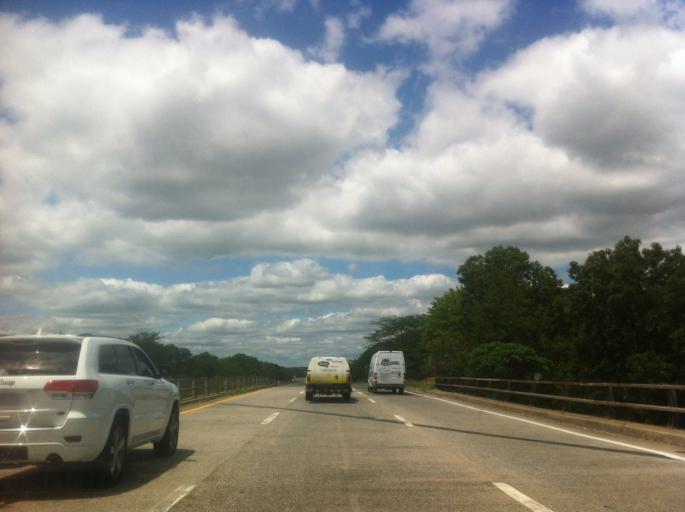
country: US
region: New York
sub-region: Suffolk County
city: Shirley
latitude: 40.8511
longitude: -72.8602
